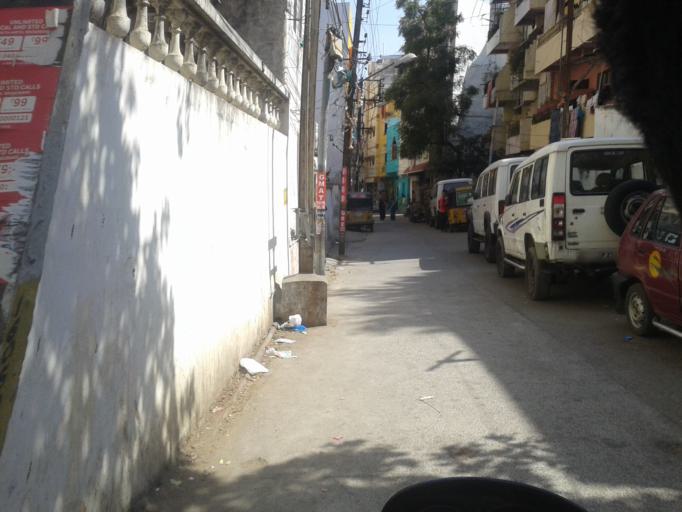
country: IN
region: Telangana
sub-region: Hyderabad
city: Hyderabad
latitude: 17.4060
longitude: 78.4820
